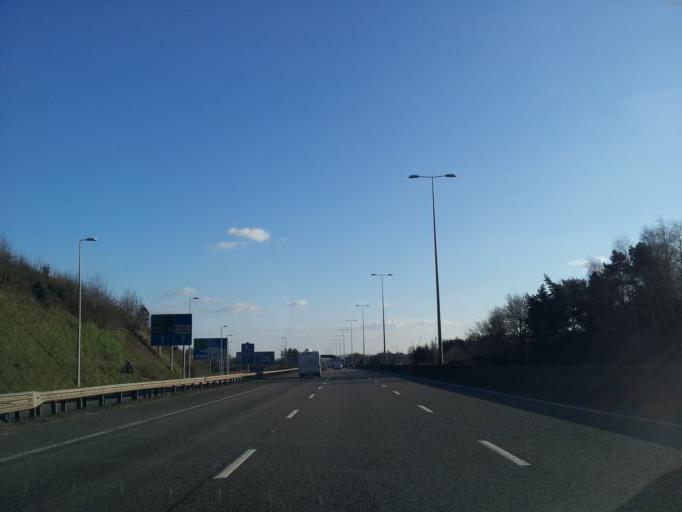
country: GB
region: England
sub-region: Devon
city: Heavitree
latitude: 50.7320
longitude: -3.4623
